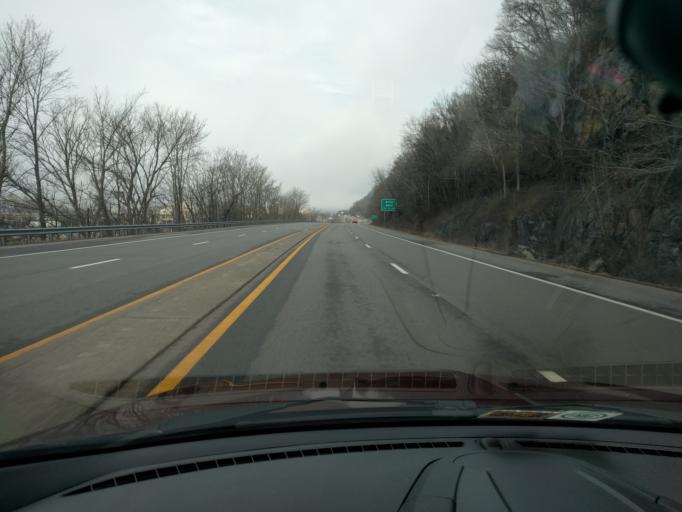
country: US
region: West Virginia
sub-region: Kanawha County
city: Belle
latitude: 38.2390
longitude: -81.5448
